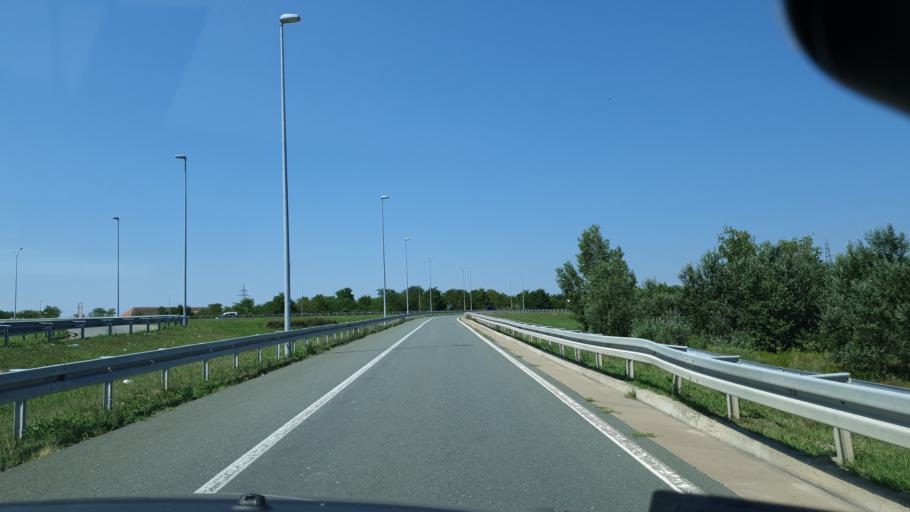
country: RS
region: Autonomna Pokrajina Vojvodina
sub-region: Juznobacki Okrug
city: Novi Sad
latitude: 45.3078
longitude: 19.8320
